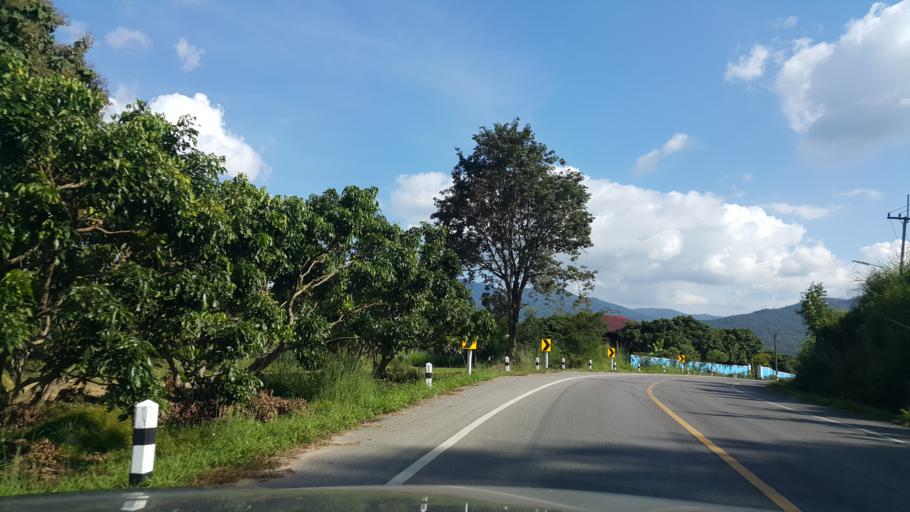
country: TH
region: Lamphun
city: Mae Tha
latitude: 18.5365
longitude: 99.2331
